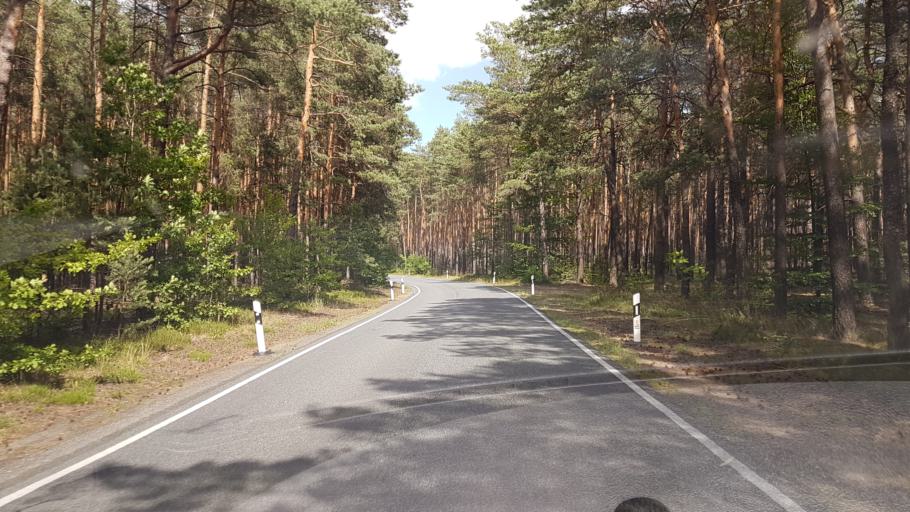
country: DE
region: Brandenburg
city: Guteborn
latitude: 51.4134
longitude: 13.9201
